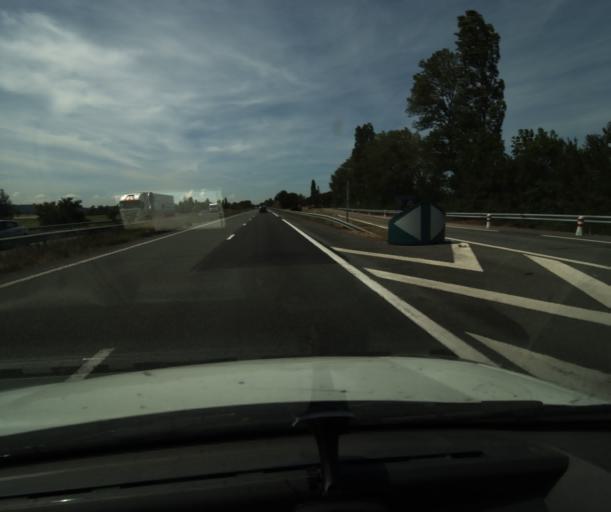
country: FR
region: Languedoc-Roussillon
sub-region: Departement de l'Aude
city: Saint-Martin-Lalande
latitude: 43.2749
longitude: 1.9956
